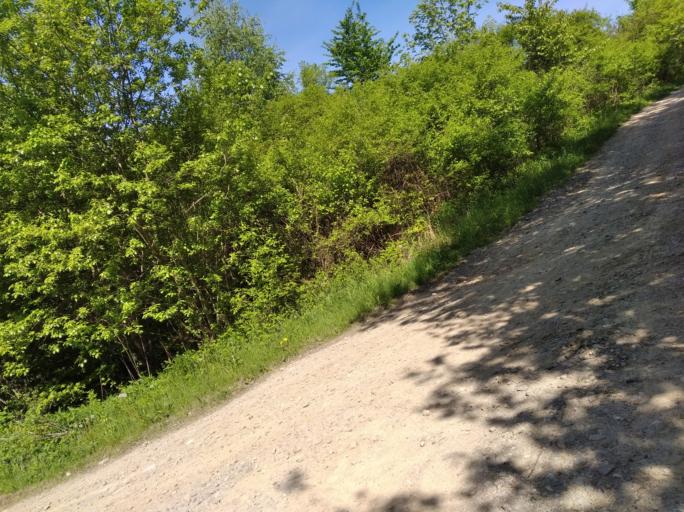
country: PL
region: Subcarpathian Voivodeship
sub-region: Powiat strzyzowski
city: Frysztak
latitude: 49.8359
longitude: 21.5559
